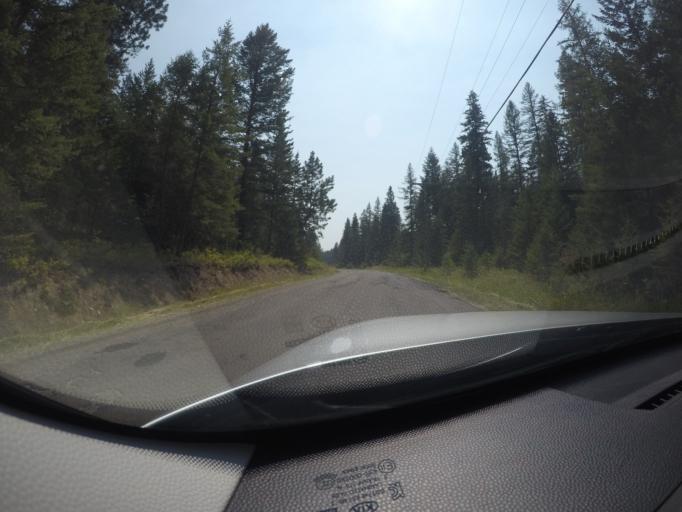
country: US
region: Montana
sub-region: Lake County
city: Polson
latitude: 47.7798
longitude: -114.1728
